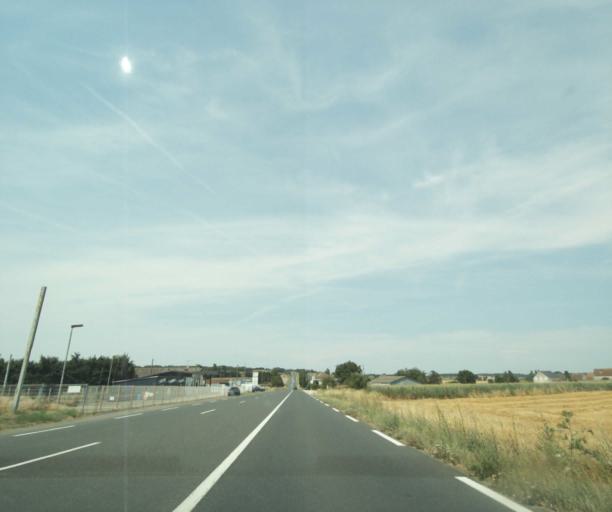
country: FR
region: Centre
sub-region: Departement d'Indre-et-Loire
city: La Celle-Saint-Avant
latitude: 47.0454
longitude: 0.6121
